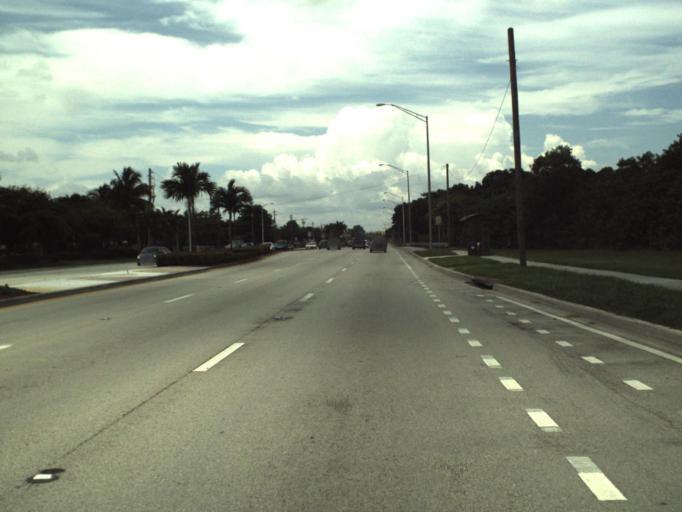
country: US
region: Florida
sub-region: Broward County
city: Margate
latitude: 26.2331
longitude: -80.1889
